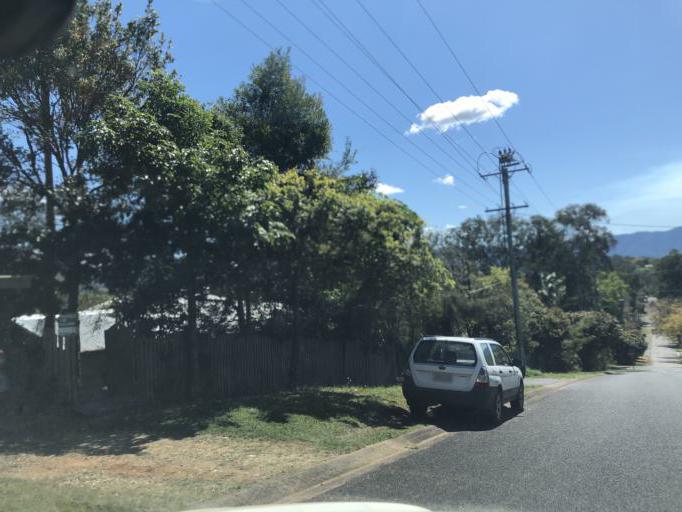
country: AU
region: New South Wales
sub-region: Bellingen
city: Bellingen
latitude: -30.4569
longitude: 152.8983
